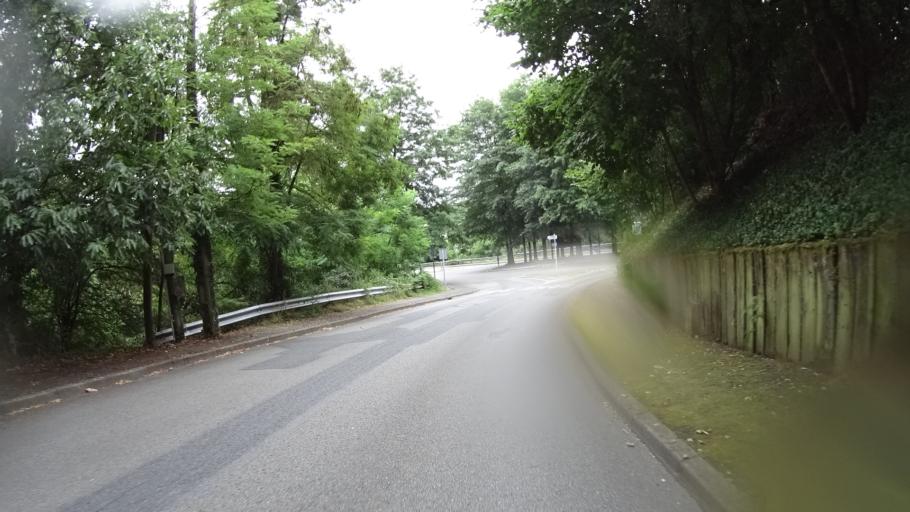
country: FR
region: Pays de la Loire
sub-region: Departement de la Loire-Atlantique
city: Bouguenais
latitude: 47.1781
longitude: -1.6371
